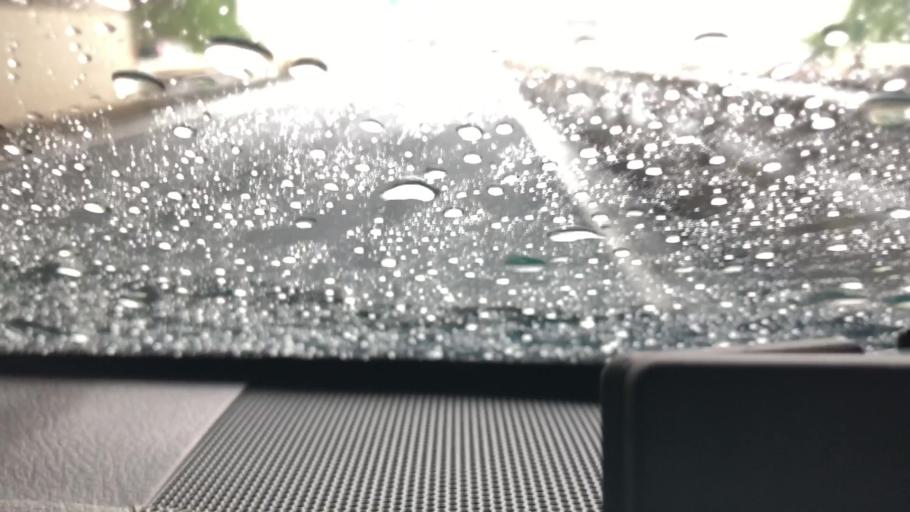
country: JP
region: Kanagawa
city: Yokohama
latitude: 35.4423
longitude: 139.5846
